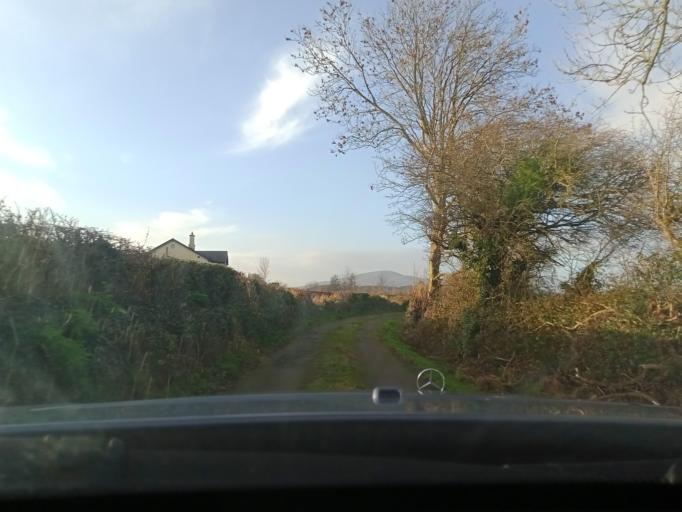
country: IE
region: Leinster
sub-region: Kilkenny
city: Callan
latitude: 52.4808
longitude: -7.4364
